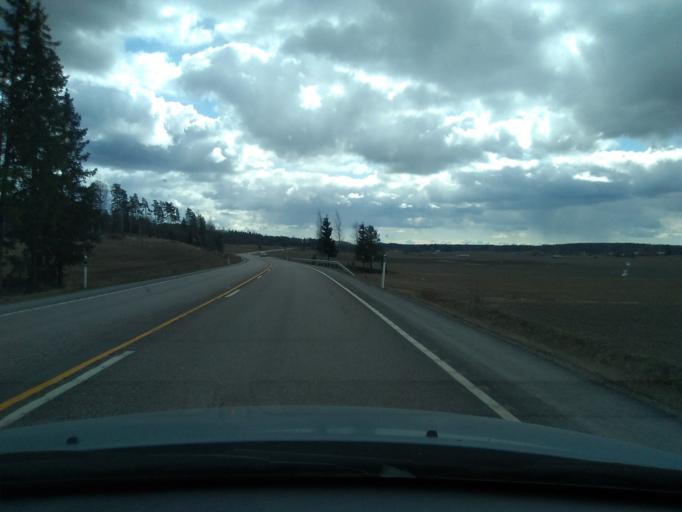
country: FI
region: Uusimaa
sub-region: Porvoo
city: Askola
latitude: 60.4869
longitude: 25.5580
